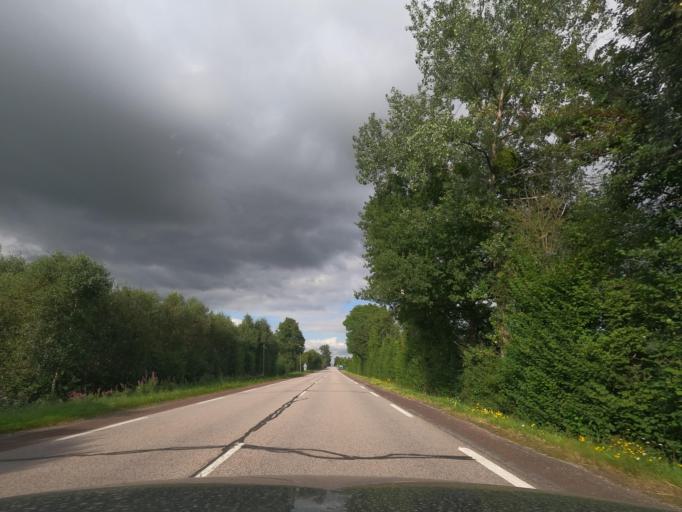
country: FR
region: Lower Normandy
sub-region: Departement de l'Orne
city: Gace
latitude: 48.8481
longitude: 0.3538
